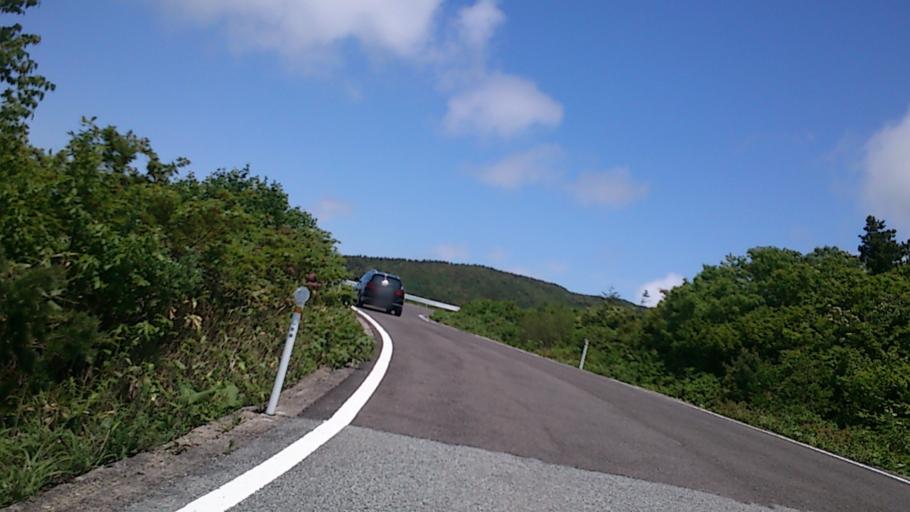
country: JP
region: Yamagata
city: Yamagata-shi
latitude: 38.1261
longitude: 140.4260
